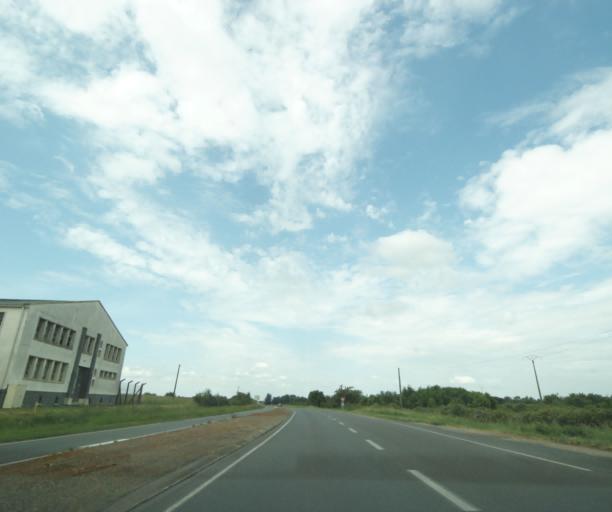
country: FR
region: Pays de la Loire
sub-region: Departement de Maine-et-Loire
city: Montreuil-Bellay
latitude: 47.1435
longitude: -0.1529
